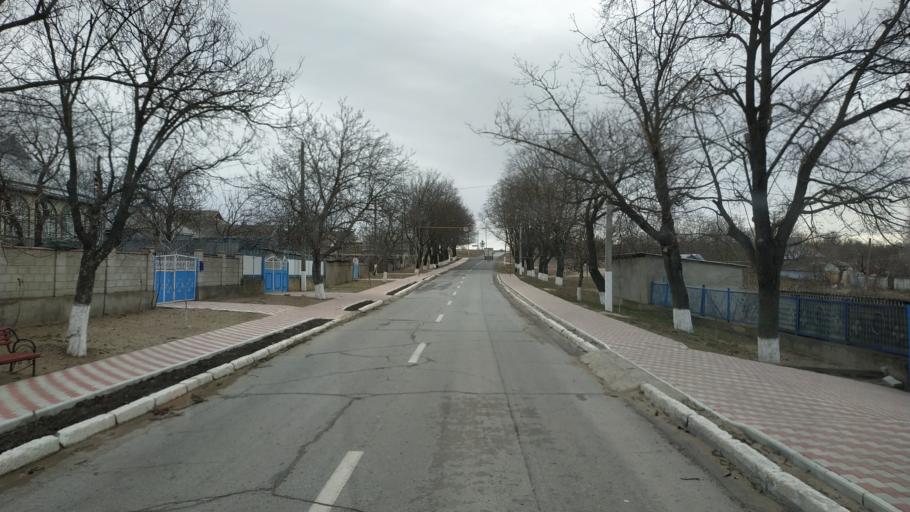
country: MD
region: Telenesti
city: Cocieri
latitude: 47.3394
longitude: 29.0968
